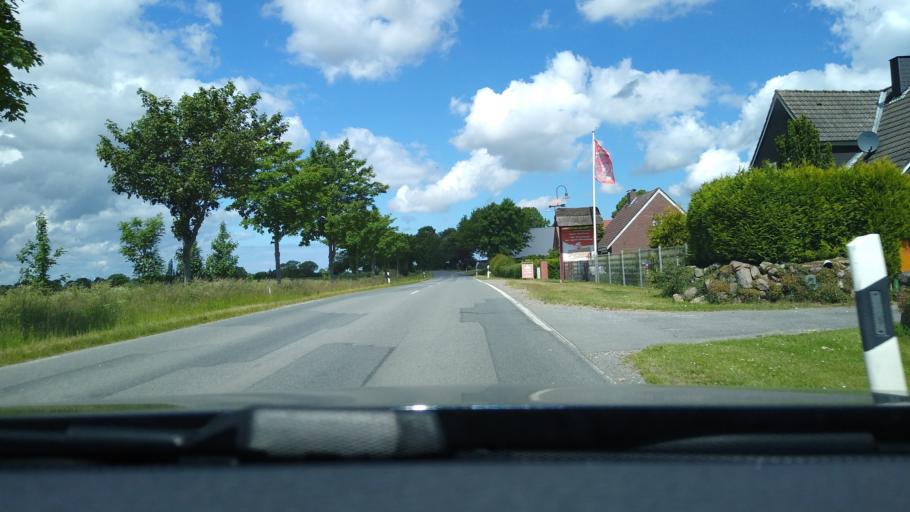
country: DE
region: Schleswig-Holstein
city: Riepsdorf
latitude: 54.2017
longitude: 10.9667
